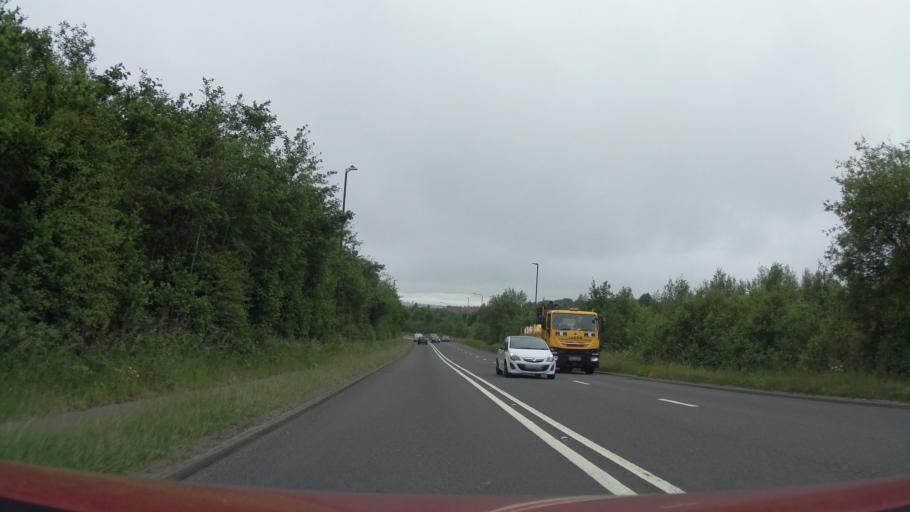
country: GB
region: England
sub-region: Derbyshire
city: Swadlincote
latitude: 52.7533
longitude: -1.5751
